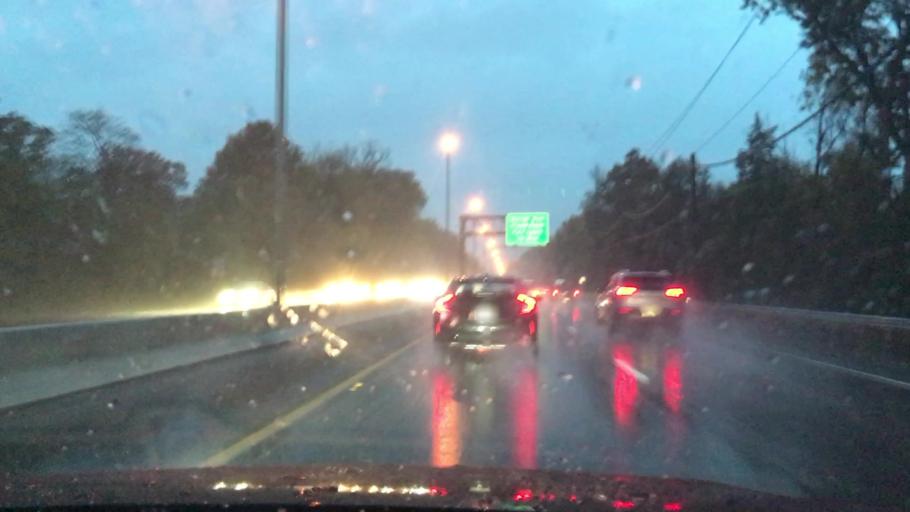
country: US
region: New Jersey
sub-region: Bergen County
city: Paramus
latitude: 40.9285
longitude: -74.0999
